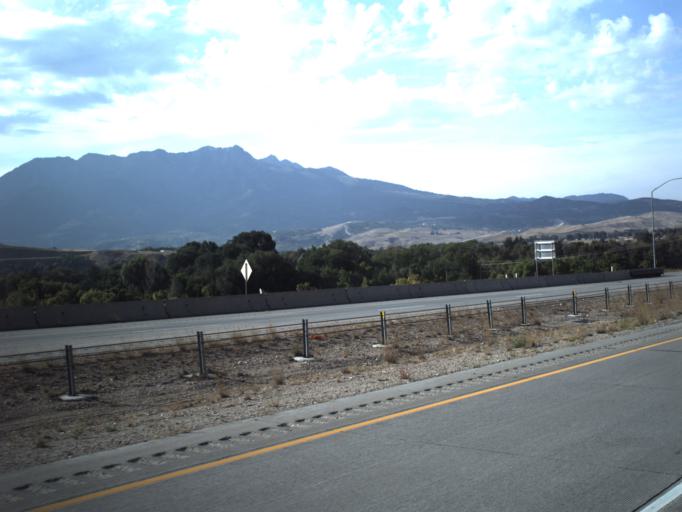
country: US
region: Utah
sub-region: Morgan County
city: Mountain Green
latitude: 41.1172
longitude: -111.7640
